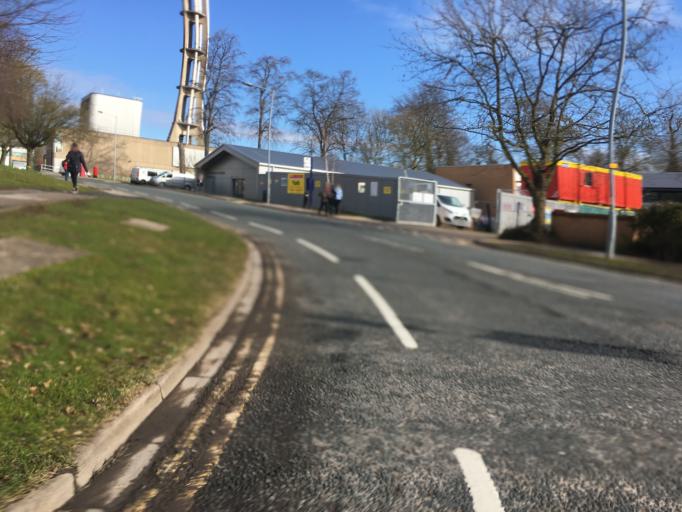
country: GB
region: England
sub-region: City of York
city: Heslington
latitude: 53.9476
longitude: -1.0476
